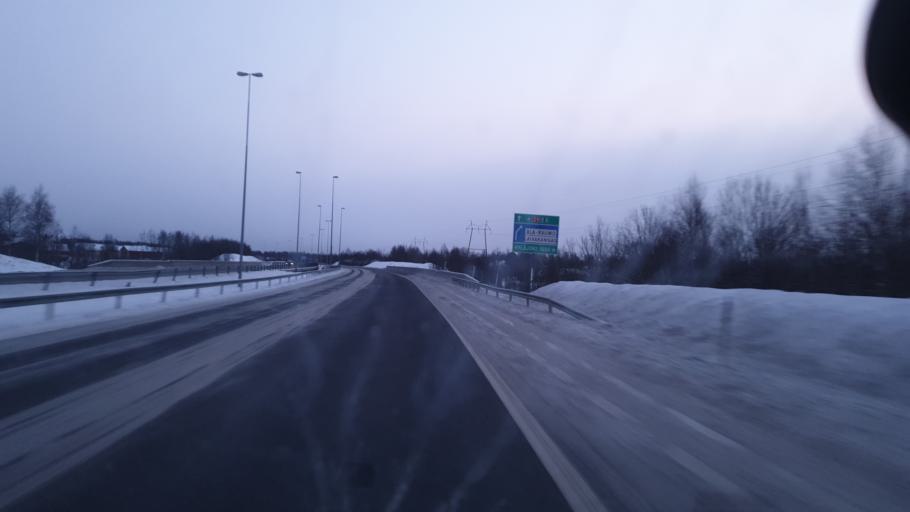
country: FI
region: Lapland
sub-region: Kemi-Tornio
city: Tornio
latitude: 65.8358
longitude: 24.2527
